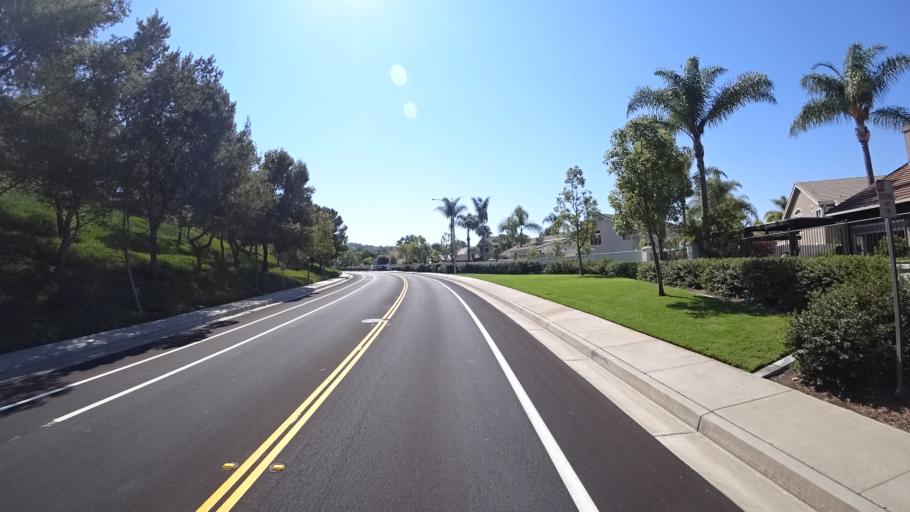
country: US
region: California
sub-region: Orange County
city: San Clemente
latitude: 33.4743
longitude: -117.6220
